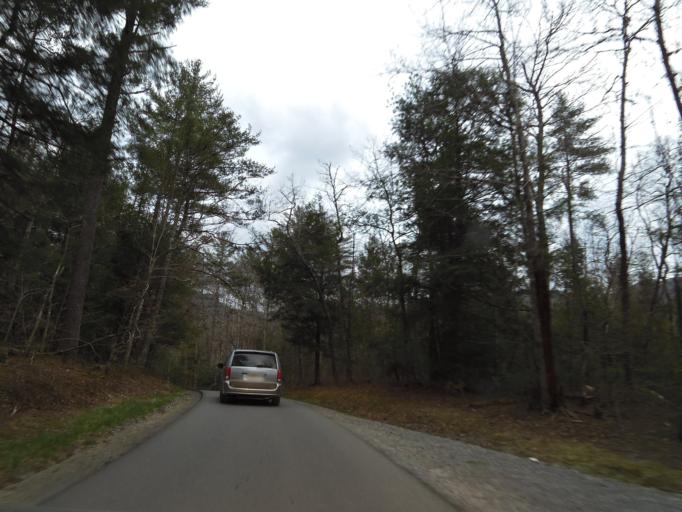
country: US
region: Tennessee
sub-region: Blount County
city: Wildwood
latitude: 35.5943
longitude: -83.7930
